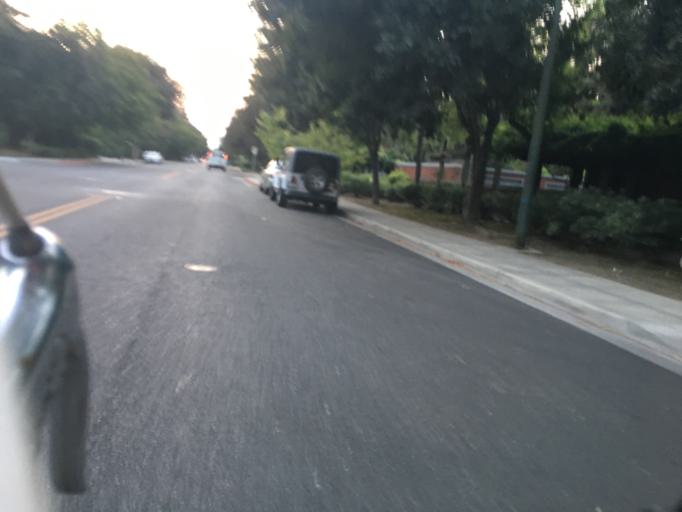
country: US
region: California
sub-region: Santa Clara County
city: Mountain View
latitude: 37.3957
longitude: -122.0714
